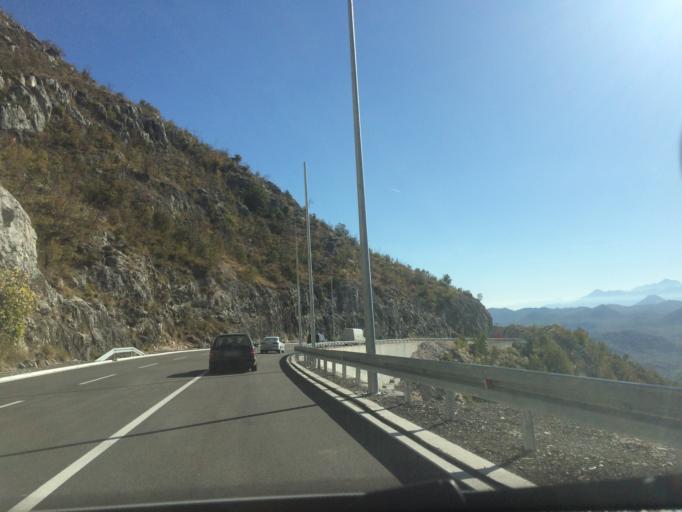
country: ME
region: Cetinje
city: Cetinje
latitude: 42.3783
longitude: 18.9750
